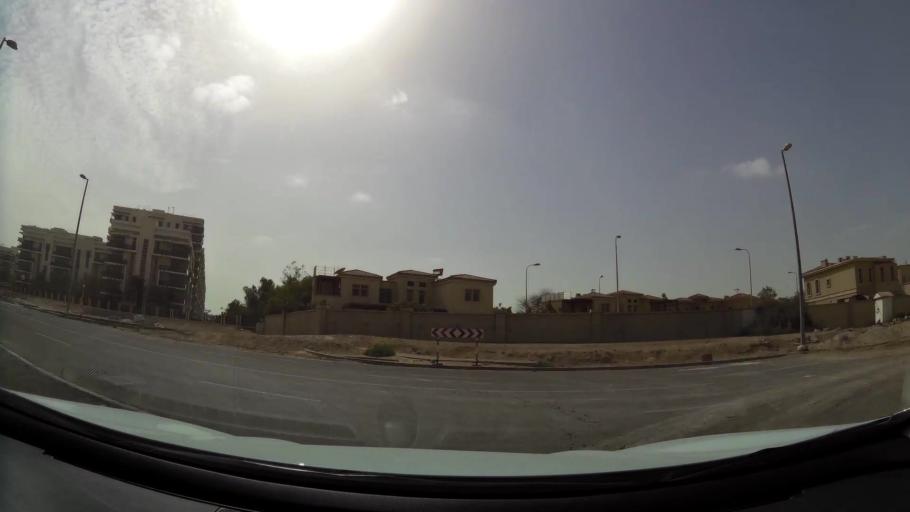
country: AE
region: Abu Dhabi
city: Abu Dhabi
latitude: 24.4154
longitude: 54.5367
